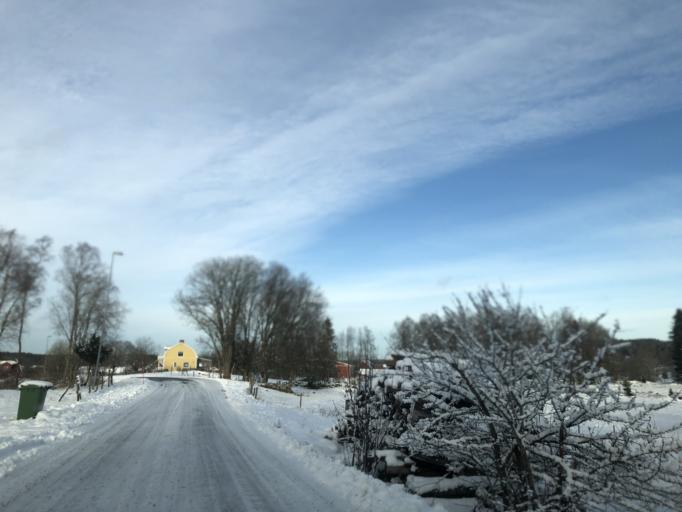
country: SE
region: Vaestra Goetaland
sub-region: Ulricehamns Kommun
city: Ulricehamn
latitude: 57.7793
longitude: 13.5241
